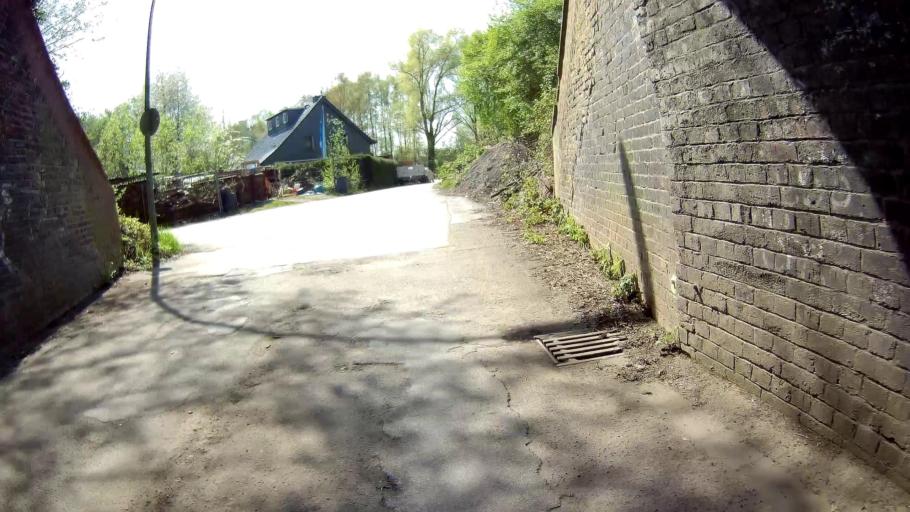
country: DE
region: North Rhine-Westphalia
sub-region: Regierungsbezirk Munster
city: Gladbeck
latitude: 51.5463
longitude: 7.0468
